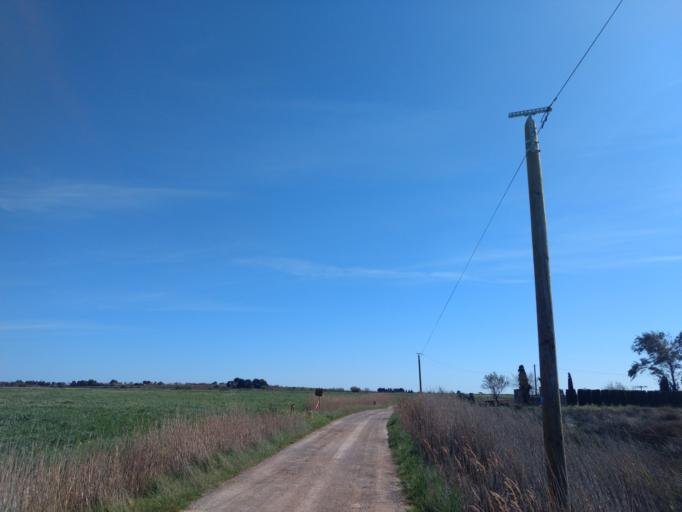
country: FR
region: Languedoc-Roussillon
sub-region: Departement de l'Herault
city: Mireval
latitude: 43.5182
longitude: 3.8343
